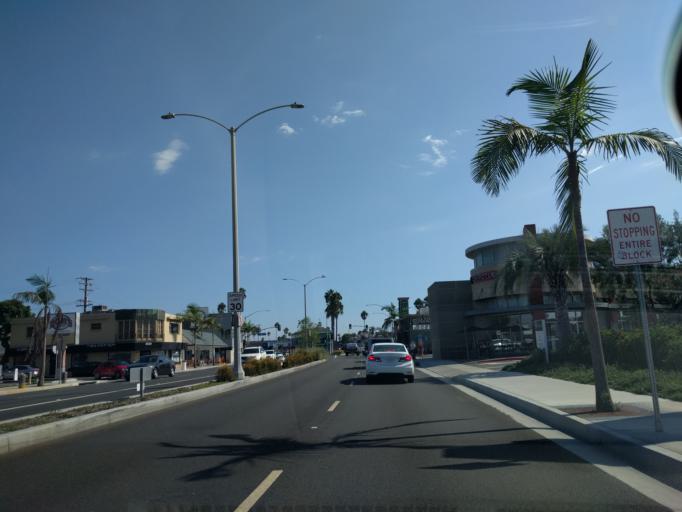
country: US
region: California
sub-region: Orange County
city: Newport Beach
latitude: 33.6157
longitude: -117.9305
